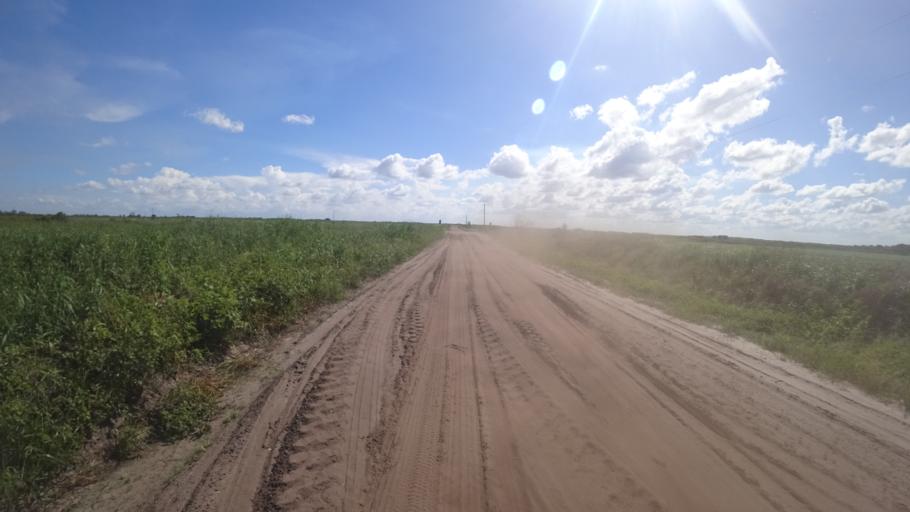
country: US
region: Florida
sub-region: DeSoto County
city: Arcadia
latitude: 27.3340
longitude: -82.0969
